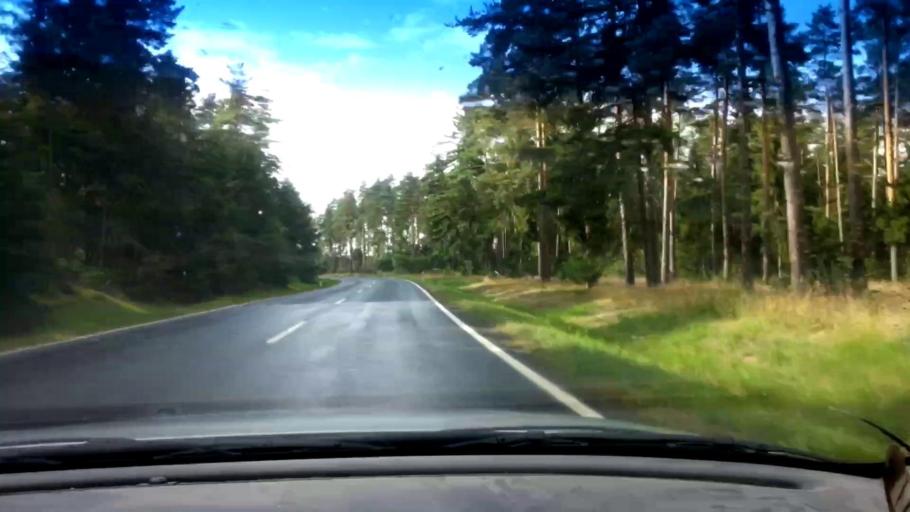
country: DE
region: Bavaria
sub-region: Upper Palatinate
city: Mitterteich
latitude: 49.9955
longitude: 12.2230
